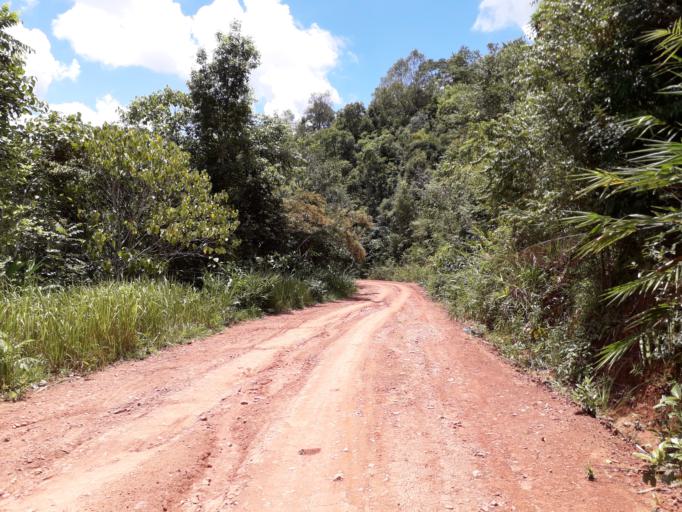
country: CN
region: Yunnan
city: Menglie
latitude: 22.2679
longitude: 101.5664
